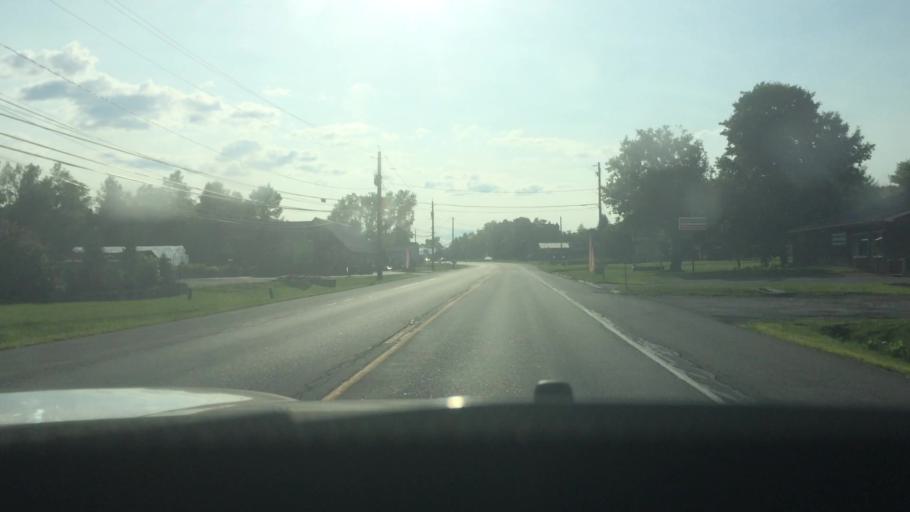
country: US
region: New York
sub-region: St. Lawrence County
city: Potsdam
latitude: 44.6675
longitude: -75.0188
